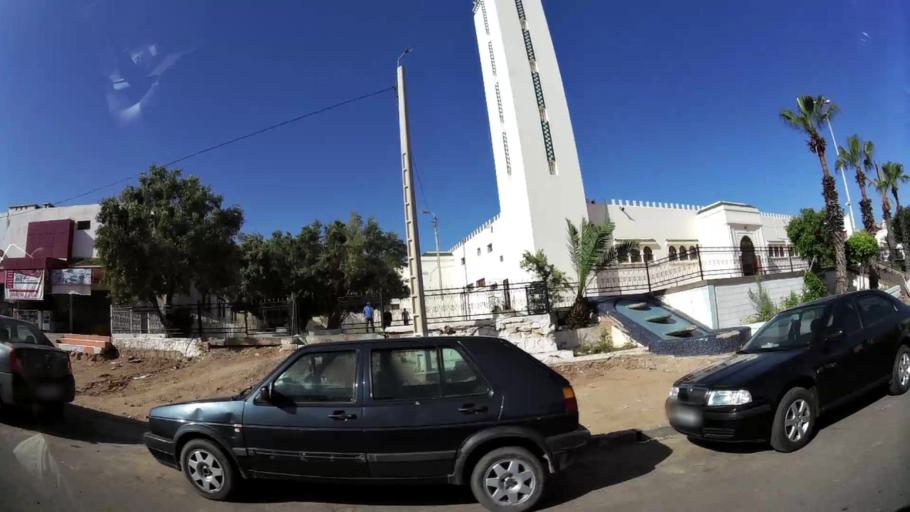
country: MA
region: Oued ed Dahab-Lagouira
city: Dakhla
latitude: 30.4194
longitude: -9.5701
